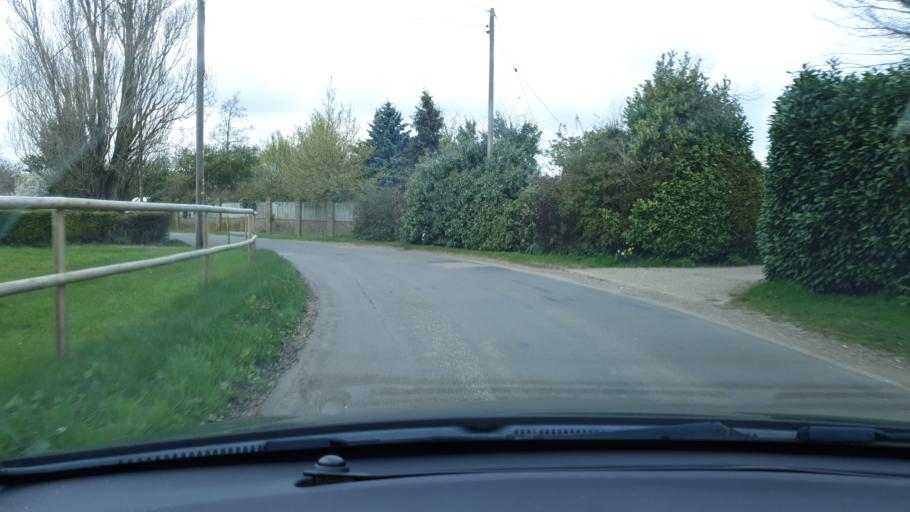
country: GB
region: England
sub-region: Essex
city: Mistley
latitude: 51.9006
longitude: 1.1371
